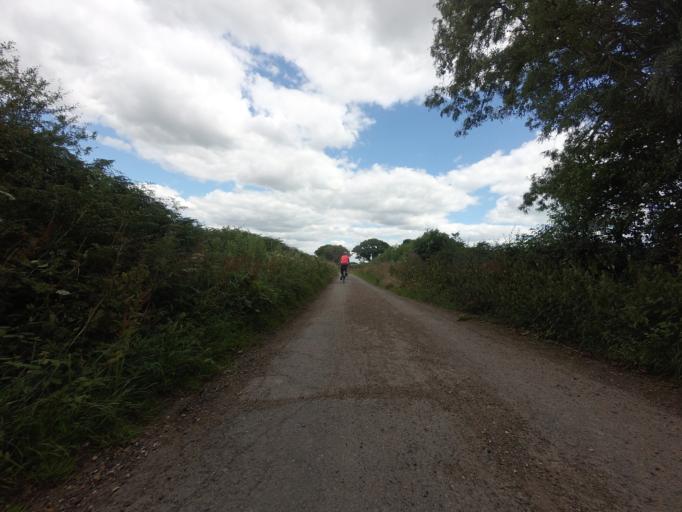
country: GB
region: England
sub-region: East Sussex
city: Hailsham
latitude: 50.8287
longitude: 0.2670
